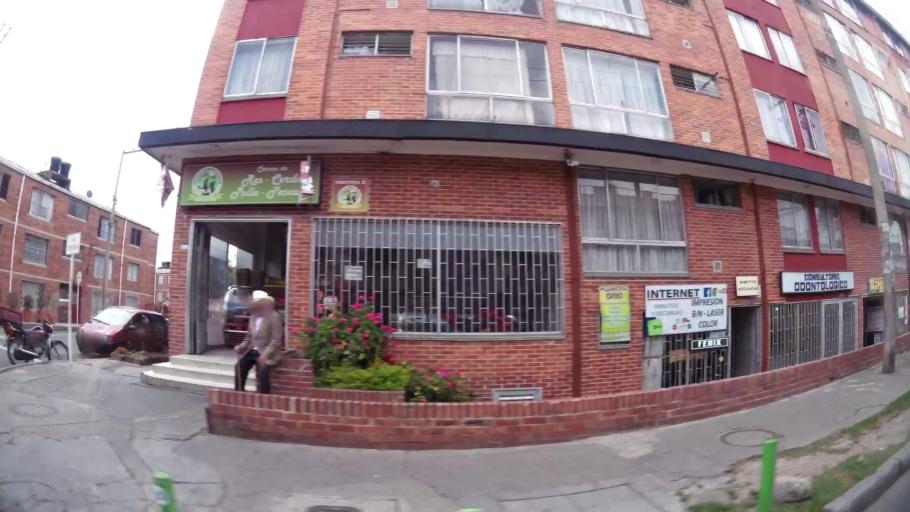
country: CO
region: Cundinamarca
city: La Calera
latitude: 4.7361
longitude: -74.0275
